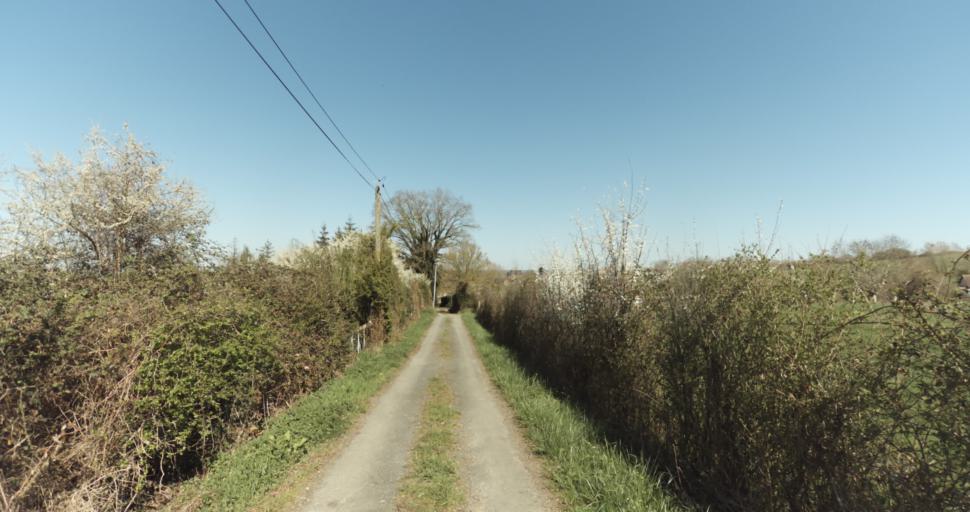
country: FR
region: Lower Normandy
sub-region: Departement du Calvados
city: Saint-Pierre-sur-Dives
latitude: 49.0154
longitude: 0.0443
